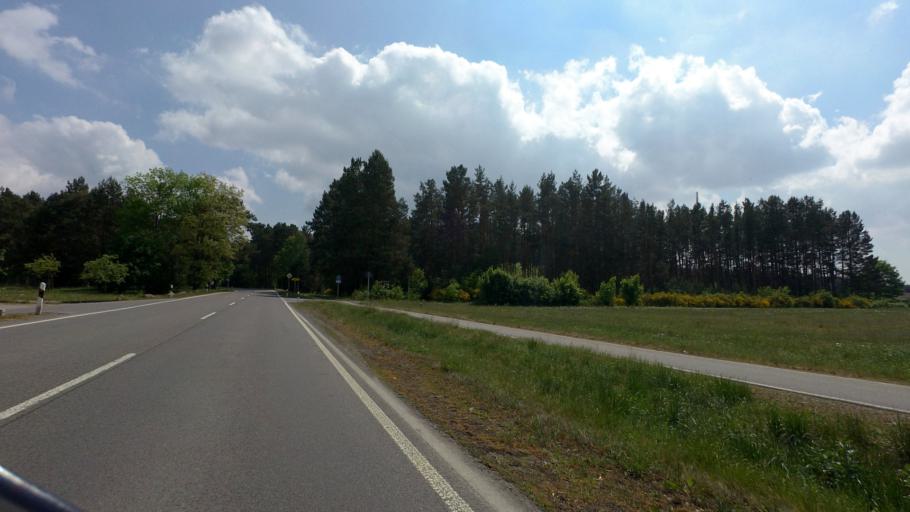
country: DE
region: Saxony
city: Weisskeissel
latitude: 51.4731
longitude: 14.7251
